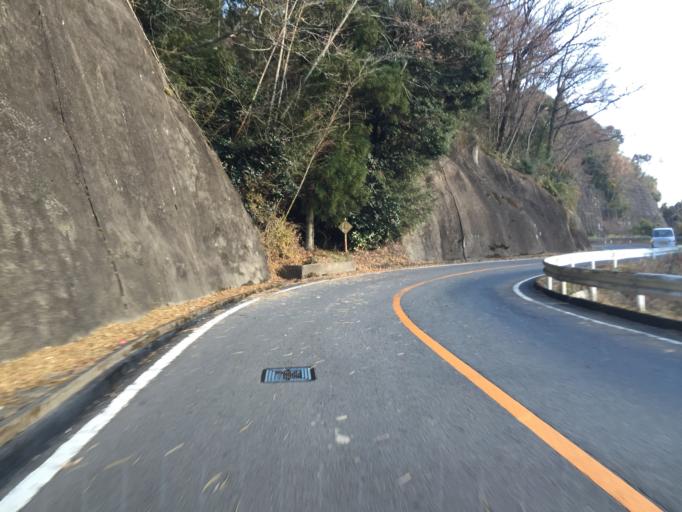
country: JP
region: Fukushima
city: Iwaki
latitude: 37.1450
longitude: 140.8371
